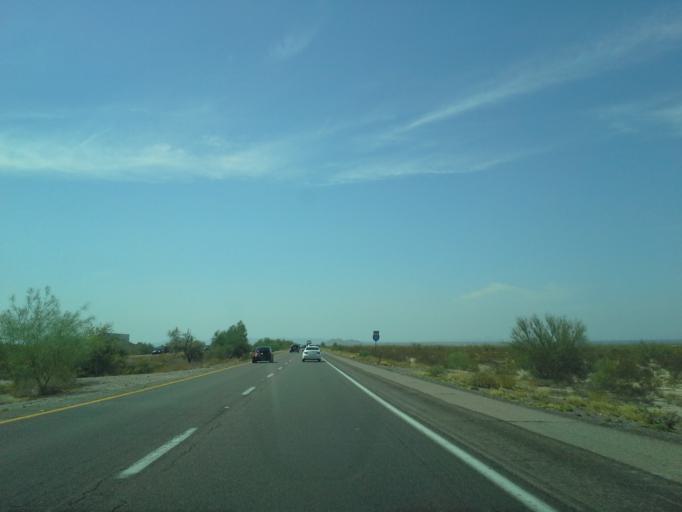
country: US
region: Arizona
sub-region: Pinal County
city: Sacaton
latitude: 33.0328
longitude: -111.7763
